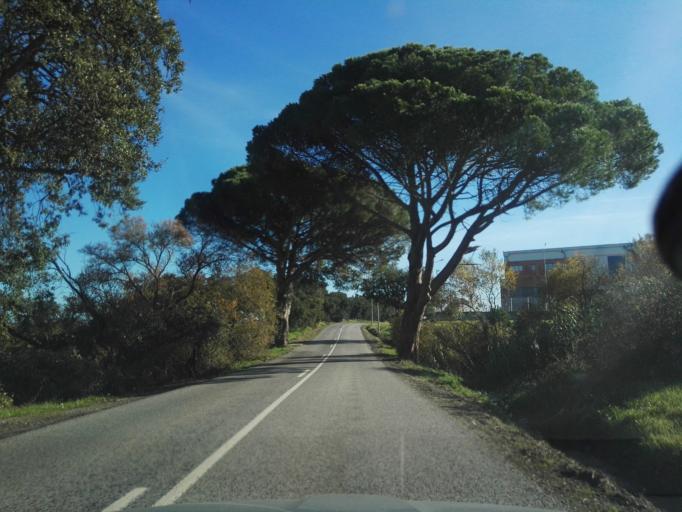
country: PT
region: Setubal
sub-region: Alcochete
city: Alcochete
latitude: 38.7281
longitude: -8.9137
